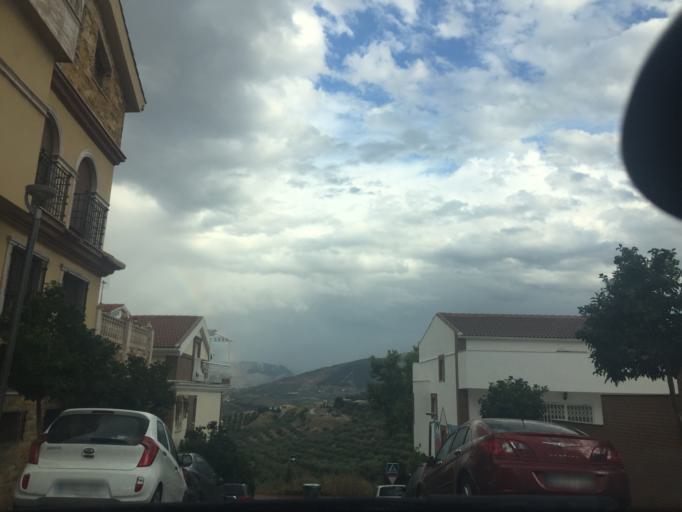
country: ES
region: Andalusia
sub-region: Provincia de Jaen
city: Jaen
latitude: 37.7748
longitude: -3.7833
